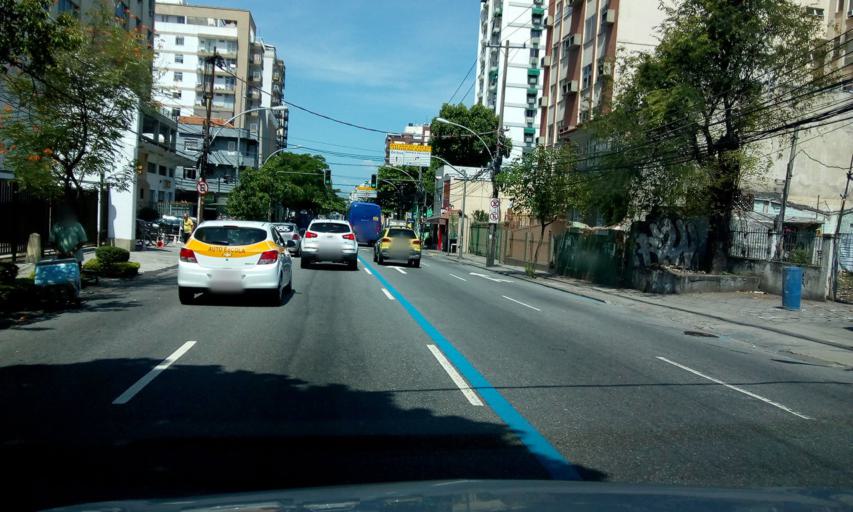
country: BR
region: Rio de Janeiro
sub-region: Rio De Janeiro
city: Rio de Janeiro
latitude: -22.9193
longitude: -43.2547
